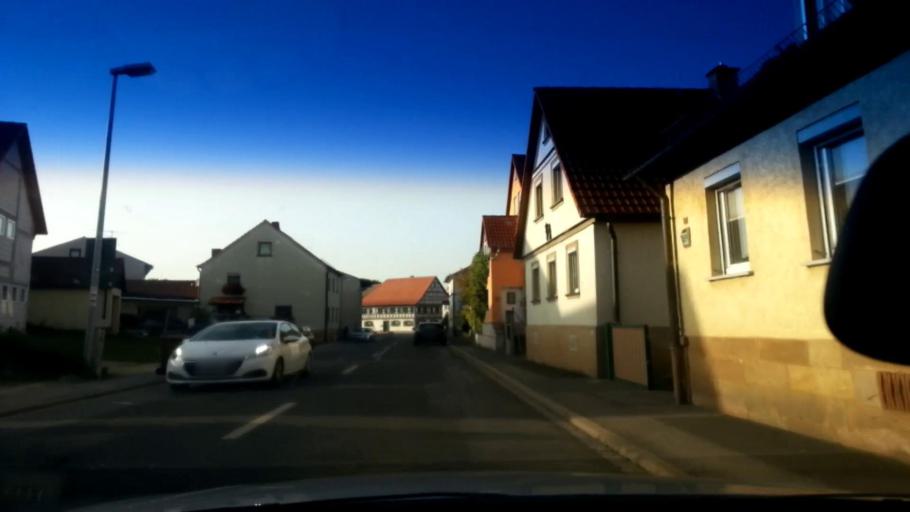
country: DE
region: Bavaria
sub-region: Upper Franconia
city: Schesslitz
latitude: 49.9746
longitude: 11.0366
